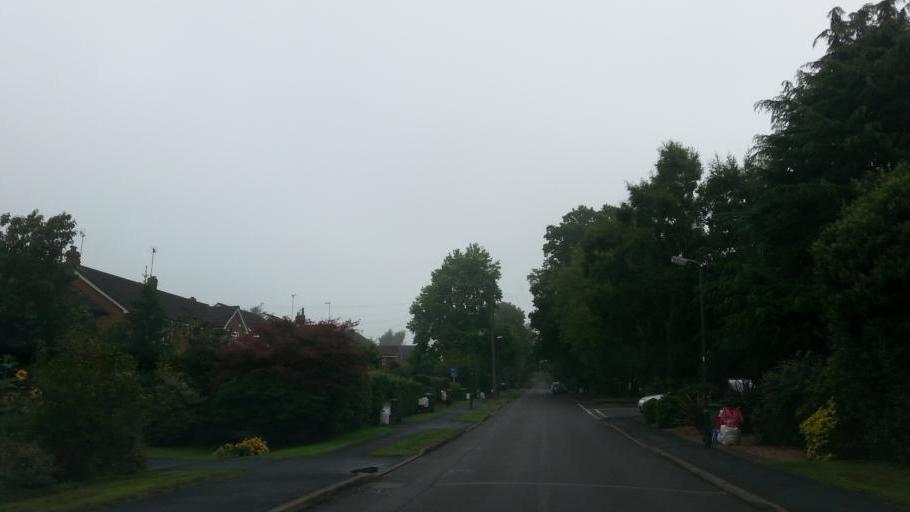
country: GB
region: England
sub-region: Warwickshire
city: Kenilworth
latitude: 52.3511
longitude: -1.5875
